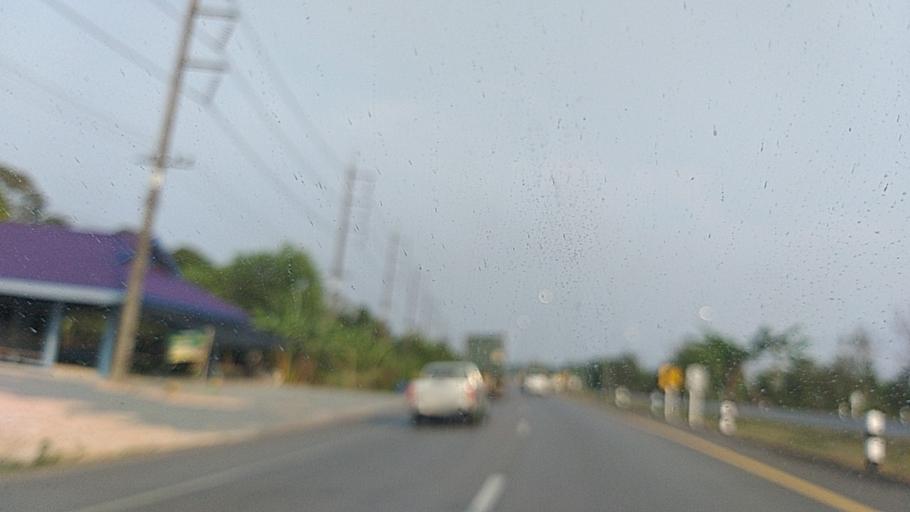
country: TH
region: Chanthaburi
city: Khlung
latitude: 12.4479
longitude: 102.2885
